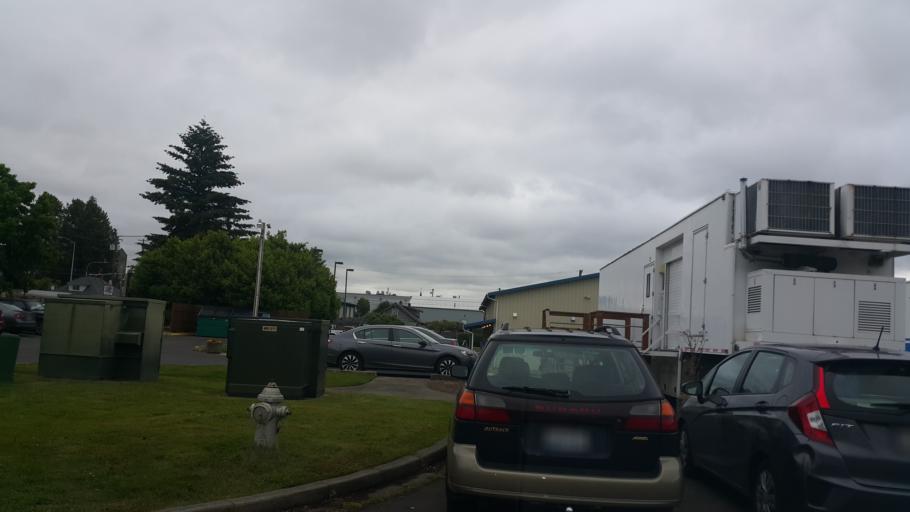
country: US
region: Washington
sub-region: Pierce County
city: Fircrest
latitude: 47.2055
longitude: -122.4891
